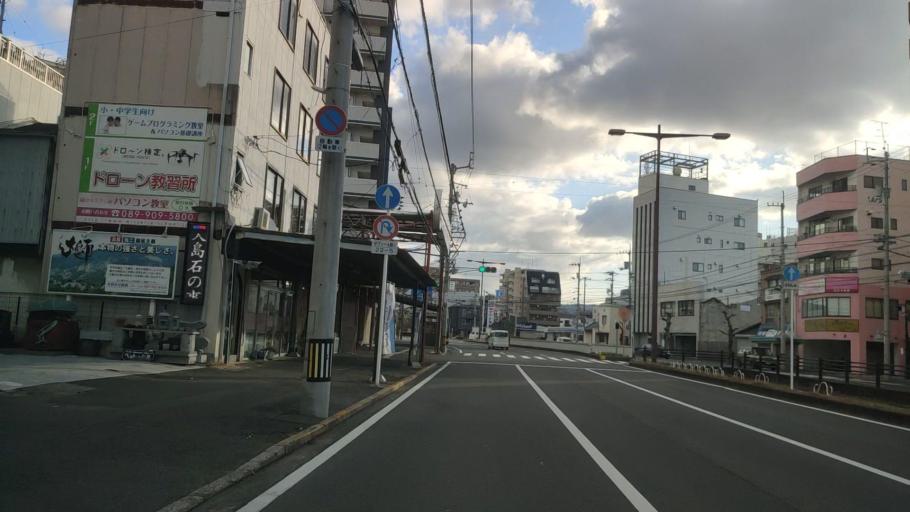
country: JP
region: Ehime
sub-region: Shikoku-chuo Shi
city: Matsuyama
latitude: 33.8350
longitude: 132.7693
